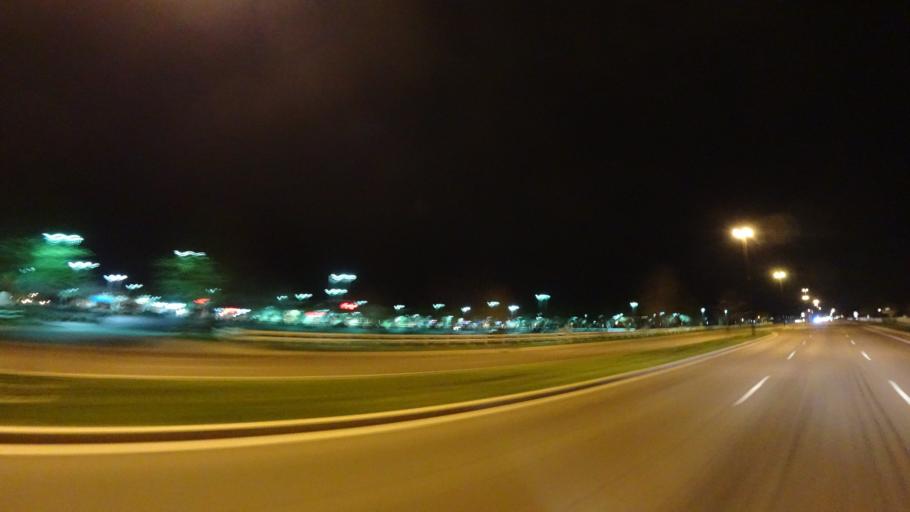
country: US
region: Arizona
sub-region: Maricopa County
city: Gilbert
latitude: 33.3491
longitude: -111.7215
